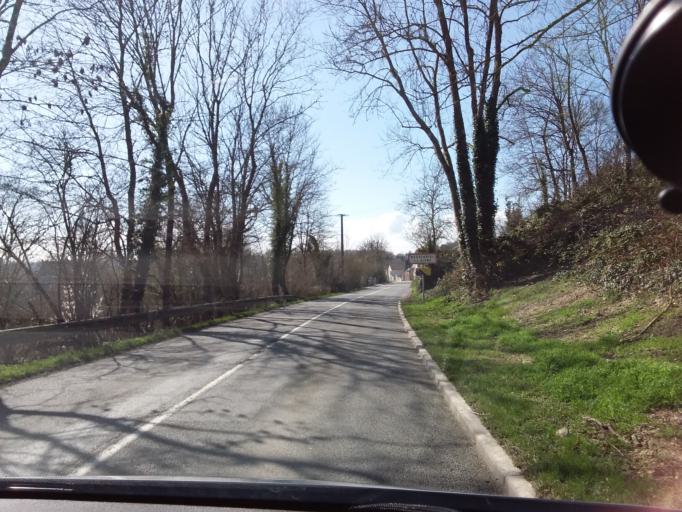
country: FR
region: Picardie
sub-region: Departement de l'Aisne
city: Guignicourt
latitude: 49.4348
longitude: 4.0322
